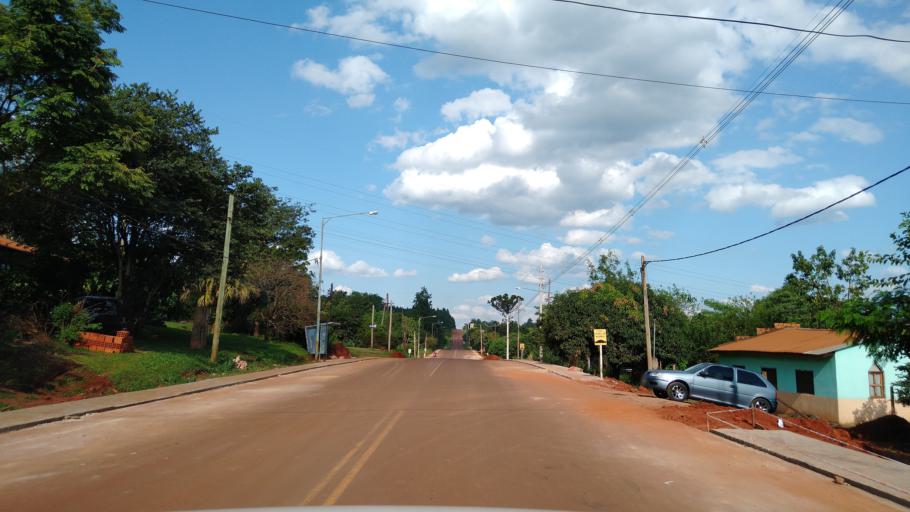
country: AR
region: Misiones
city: Puerto Piray
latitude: -26.4701
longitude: -54.6949
